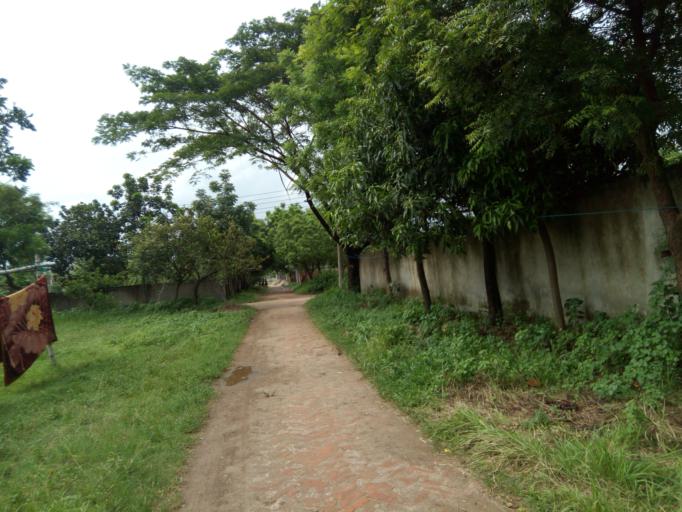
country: BD
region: Dhaka
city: Azimpur
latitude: 23.7530
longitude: 90.3416
